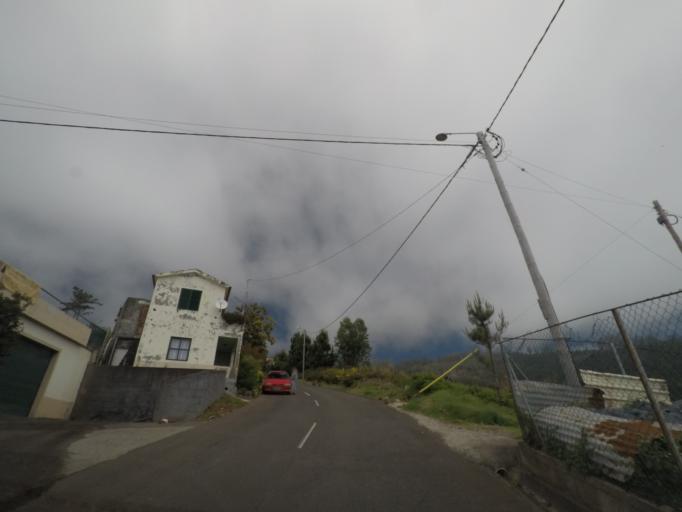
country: PT
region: Madeira
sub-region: Calheta
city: Arco da Calheta
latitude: 32.7171
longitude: -17.1248
